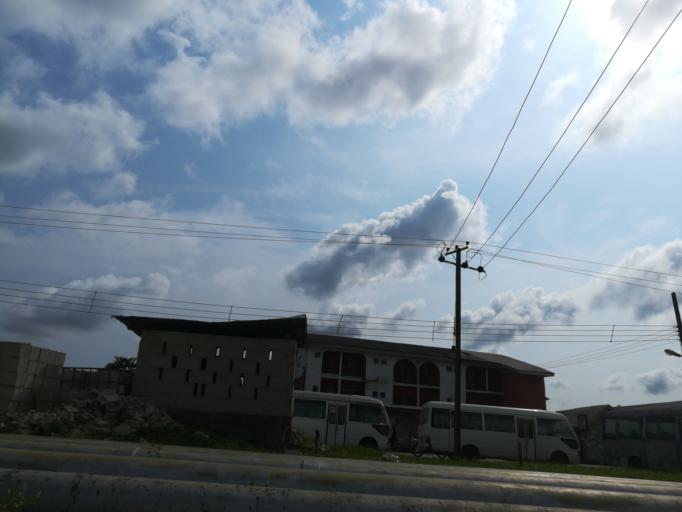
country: NG
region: Rivers
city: Okrika
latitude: 4.7531
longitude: 7.0994
